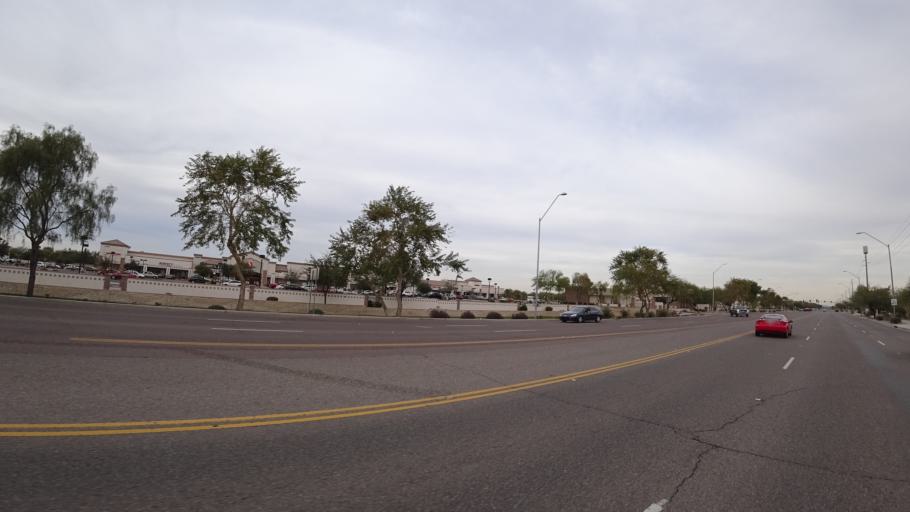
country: US
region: Arizona
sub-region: Maricopa County
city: Surprise
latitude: 33.6091
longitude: -112.3581
